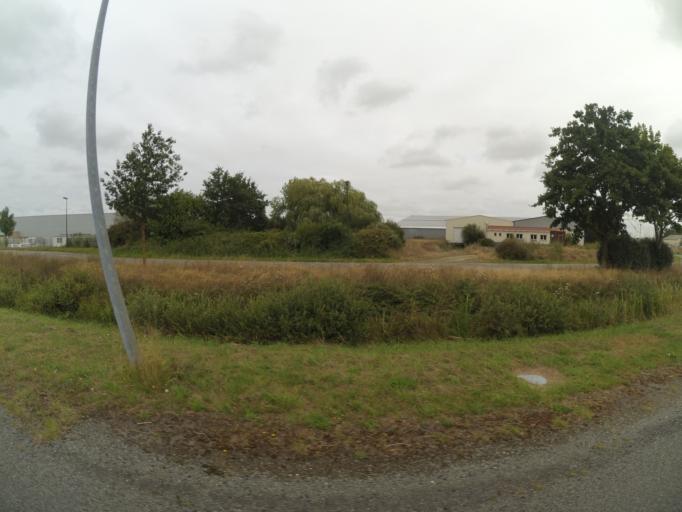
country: FR
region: Pays de la Loire
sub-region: Departement de la Loire-Atlantique
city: Lege
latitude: 46.8920
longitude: -1.5980
